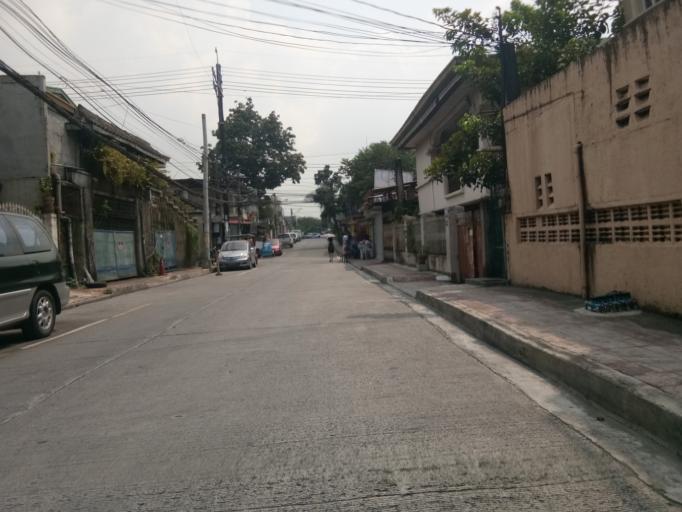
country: PH
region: Metro Manila
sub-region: San Juan
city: San Juan
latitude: 14.6150
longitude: 121.0555
